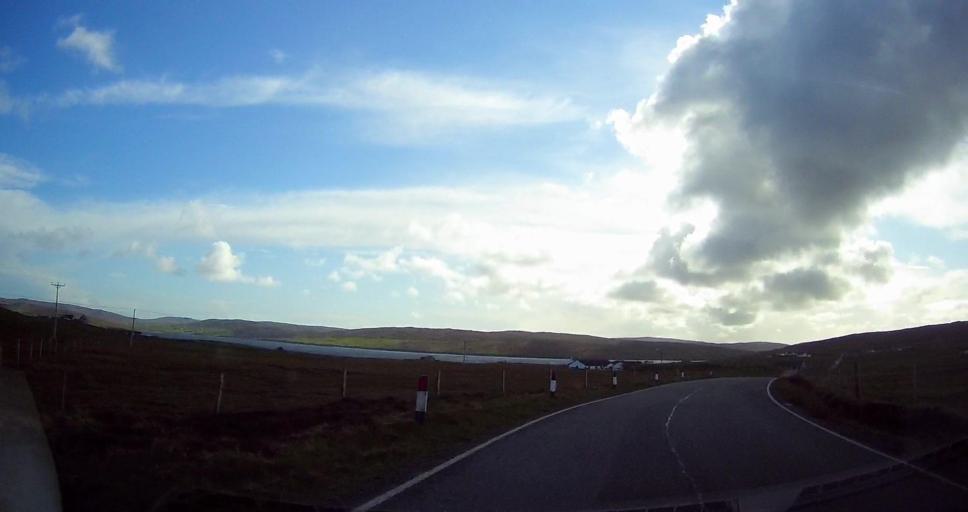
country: GB
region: Scotland
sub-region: Shetland Islands
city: Shetland
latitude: 60.3567
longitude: -1.1461
